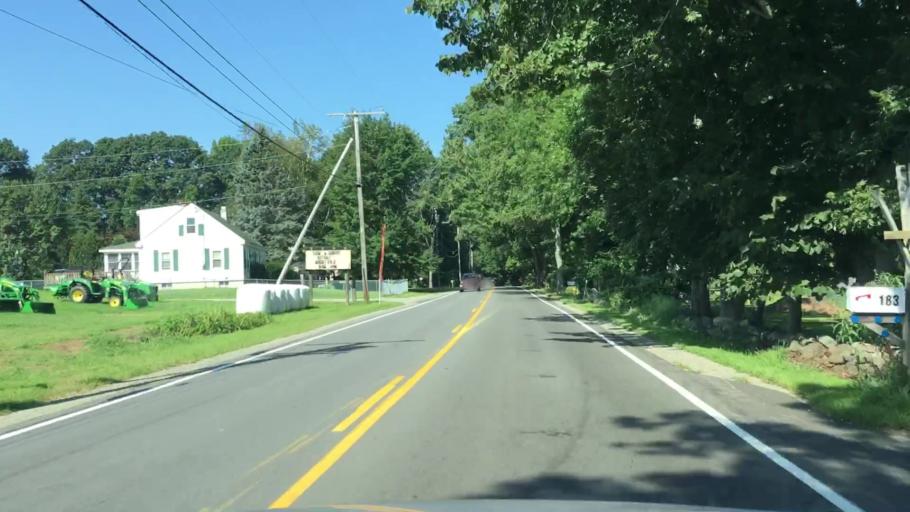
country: US
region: New Hampshire
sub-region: Rockingham County
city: Kensington
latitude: 42.9094
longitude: -70.9528
